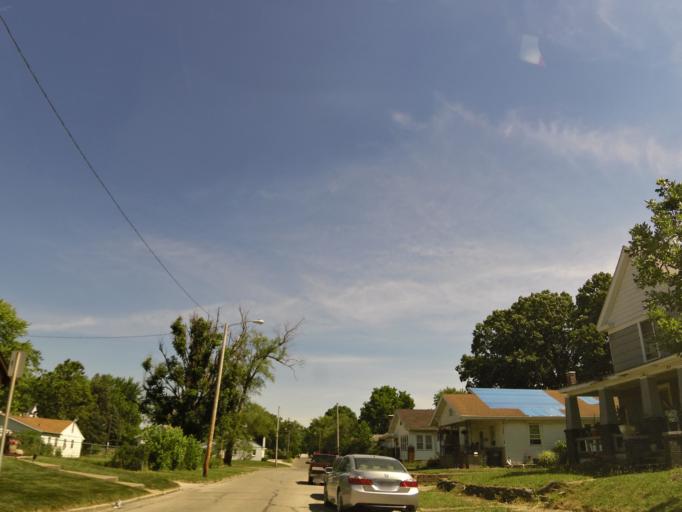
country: US
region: Illinois
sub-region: Vermilion County
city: Danville
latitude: 40.1304
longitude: -87.6065
